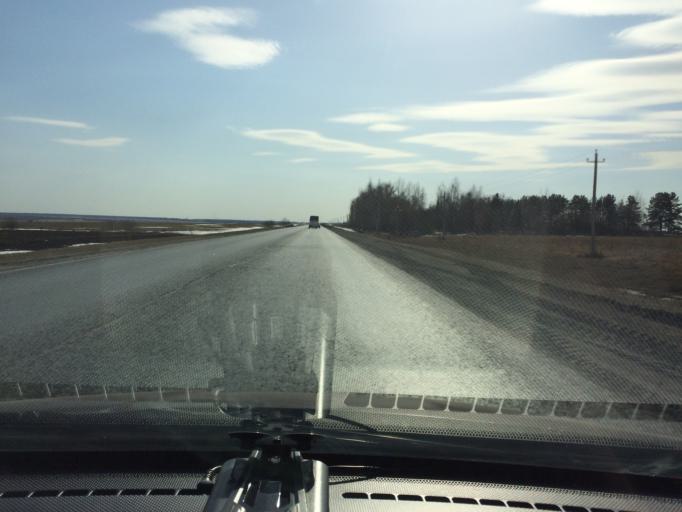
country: RU
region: Mariy-El
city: Yoshkar-Ola
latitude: 56.7044
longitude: 48.0744
